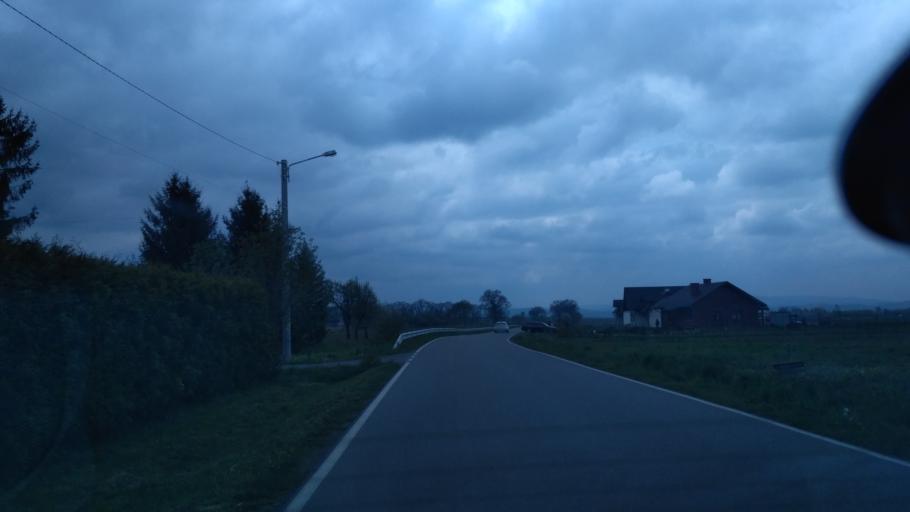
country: PL
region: Subcarpathian Voivodeship
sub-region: Powiat brzozowski
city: Turze Pole
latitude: 49.6566
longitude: 21.9958
